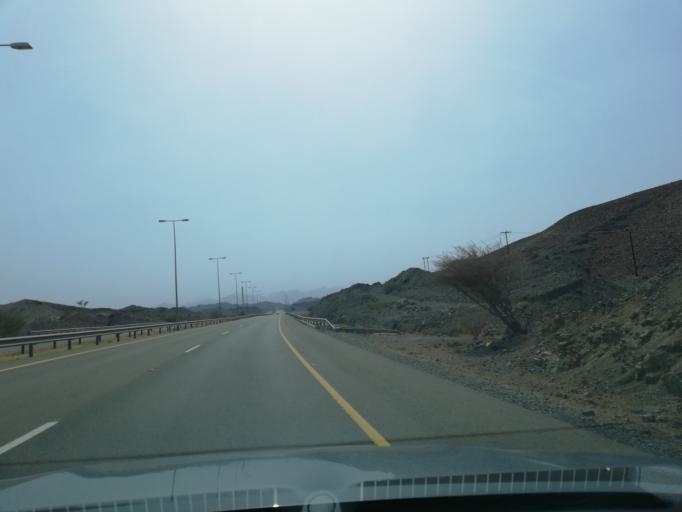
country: OM
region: Al Batinah
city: Al Liwa'
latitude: 24.3072
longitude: 56.4428
